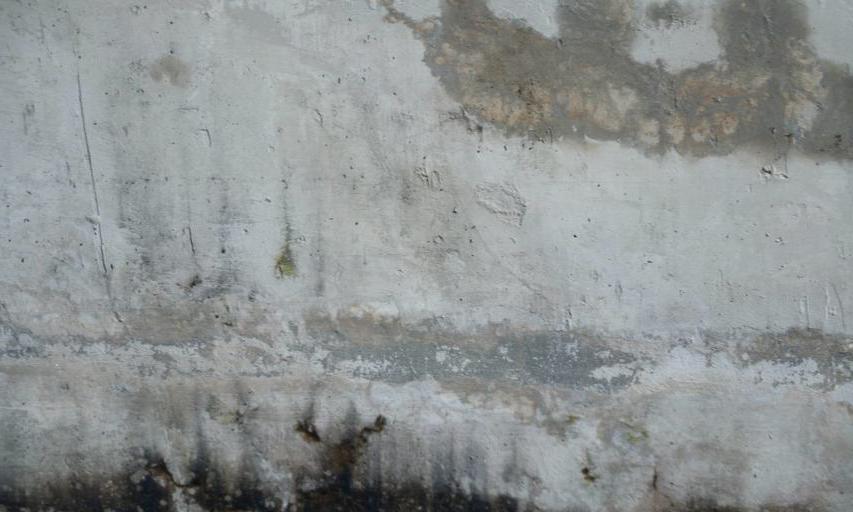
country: PT
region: Guarda
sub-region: Seia
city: Seia
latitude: 40.4703
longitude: -7.6226
